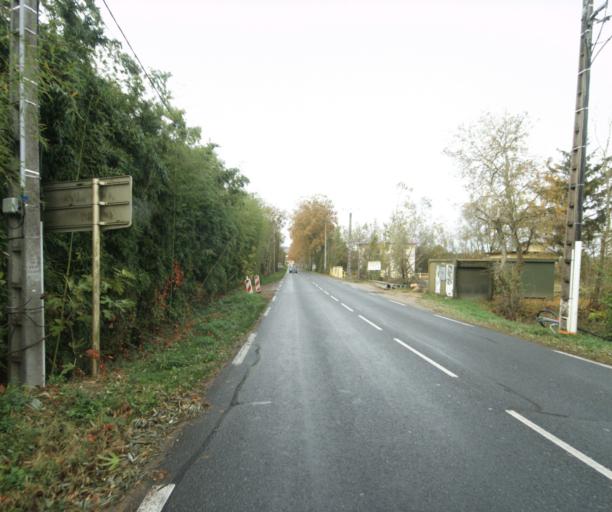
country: FR
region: Rhone-Alpes
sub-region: Departement de l'Ain
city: Pont-de-Vaux
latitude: 46.4481
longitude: 4.8938
